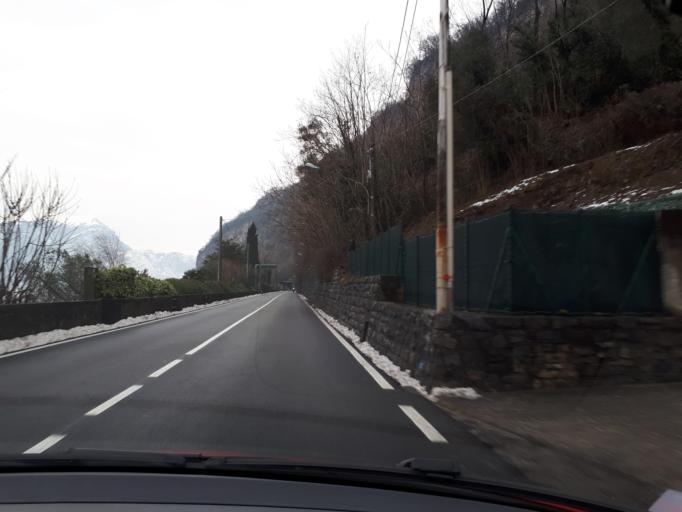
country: IT
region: Lombardy
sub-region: Provincia di Lecco
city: Lierna
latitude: 45.9407
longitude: 9.3123
